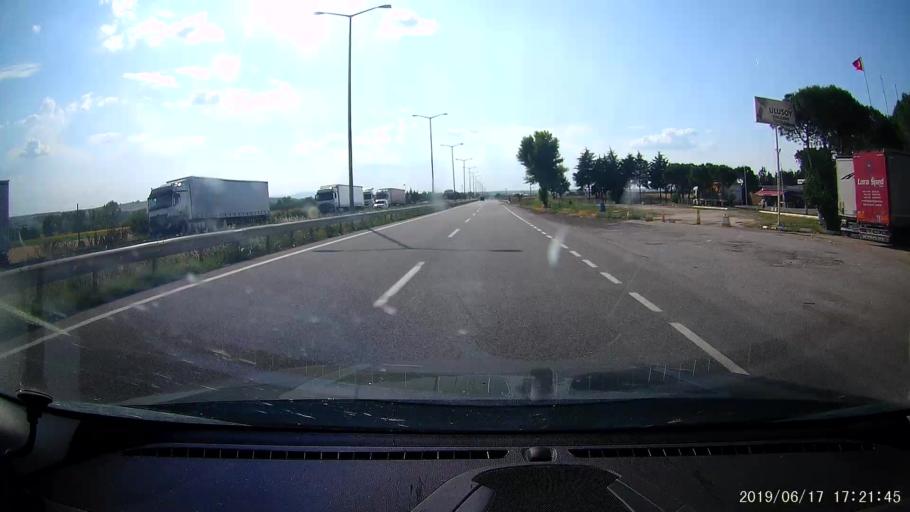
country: GR
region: East Macedonia and Thrace
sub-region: Nomos Evrou
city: Rizia
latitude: 41.7081
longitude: 26.3880
